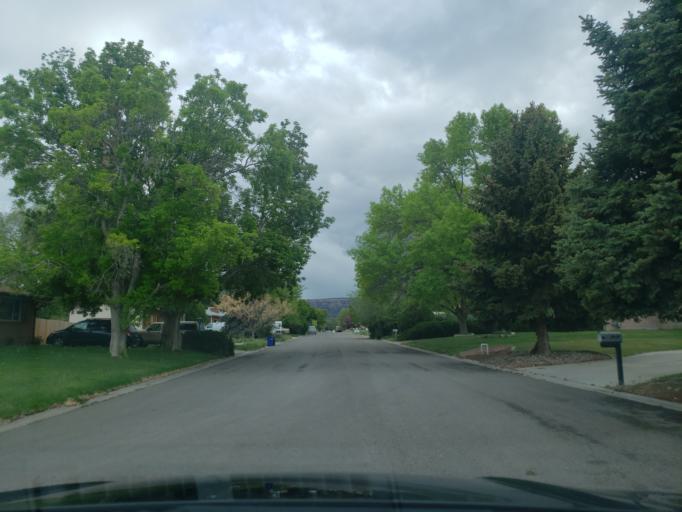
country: US
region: Colorado
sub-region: Mesa County
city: Redlands
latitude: 39.0989
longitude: -108.6584
